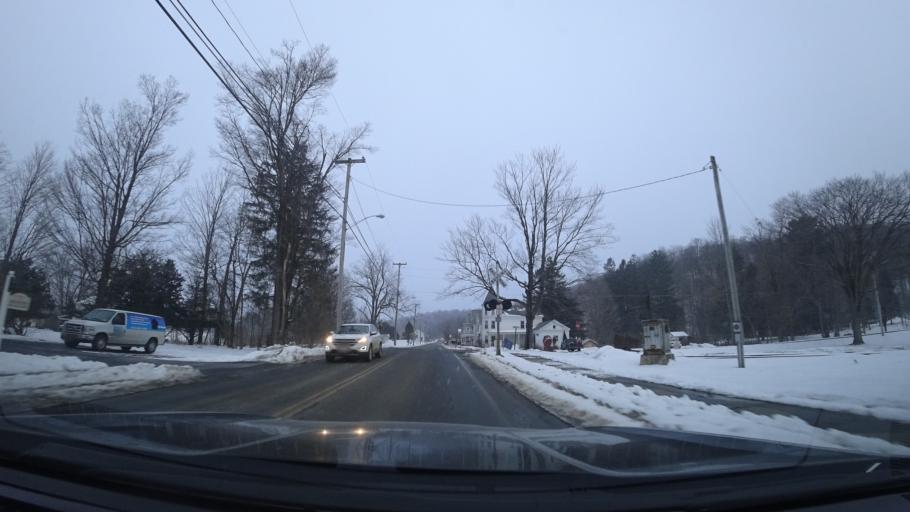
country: US
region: New York
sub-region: Washington County
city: Cambridge
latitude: 43.1712
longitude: -73.3322
